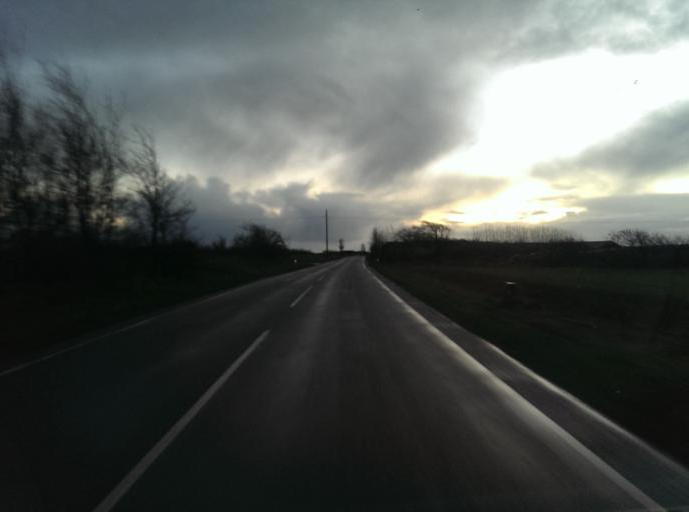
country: DK
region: South Denmark
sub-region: Esbjerg Kommune
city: Bramming
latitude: 55.4413
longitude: 8.6892
